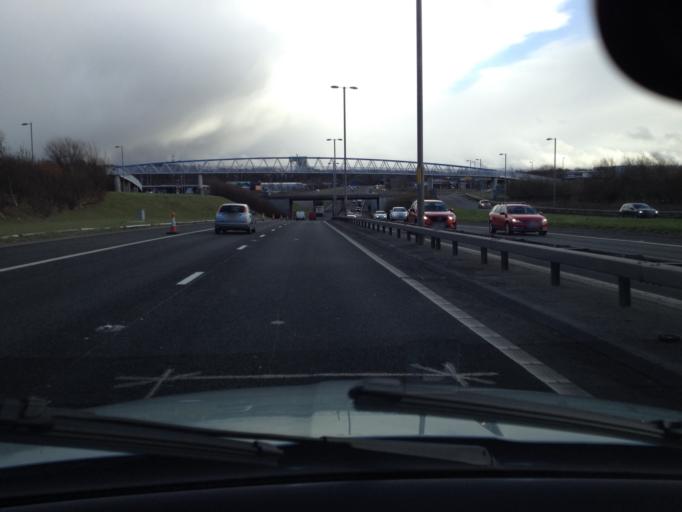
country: GB
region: Scotland
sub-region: Edinburgh
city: Newbridge
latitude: 55.9415
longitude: -3.4034
